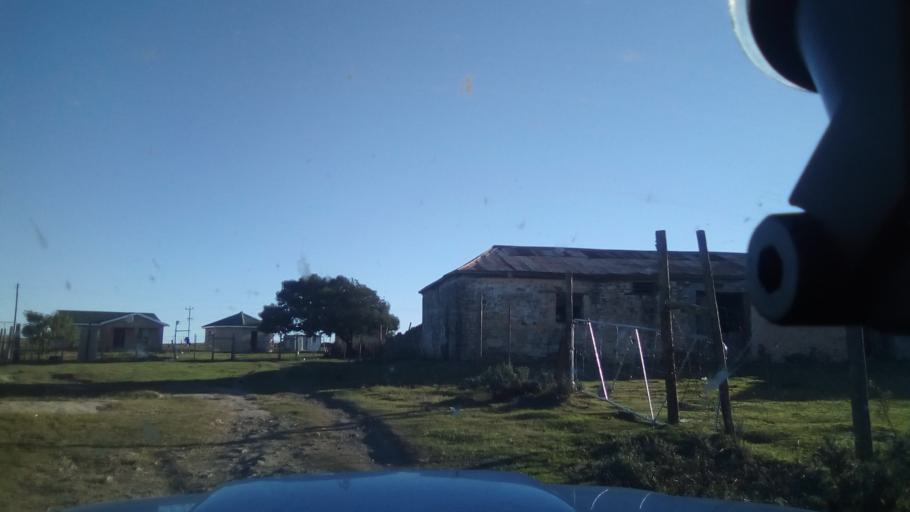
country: ZA
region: Eastern Cape
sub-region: Buffalo City Metropolitan Municipality
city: Bhisho
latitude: -32.9521
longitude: 27.2936
